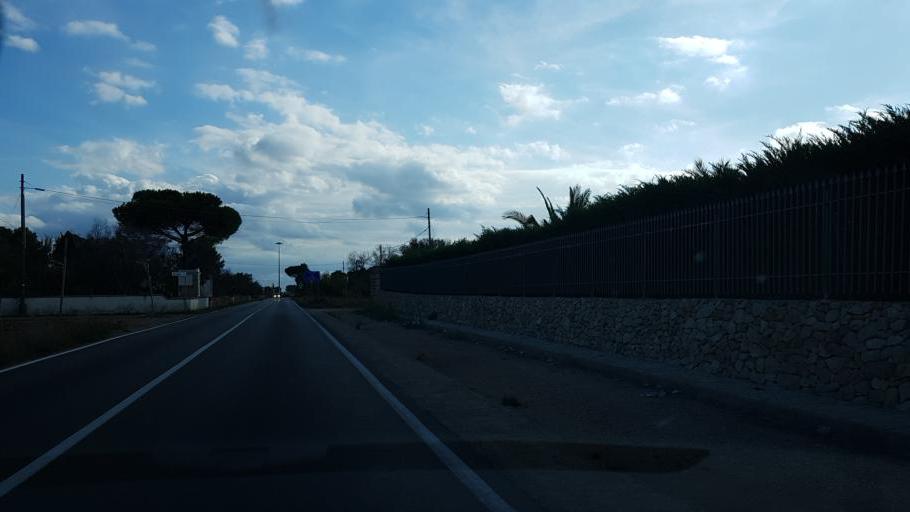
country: IT
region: Apulia
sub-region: Provincia di Lecce
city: Nardo
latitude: 40.1316
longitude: 18.0193
